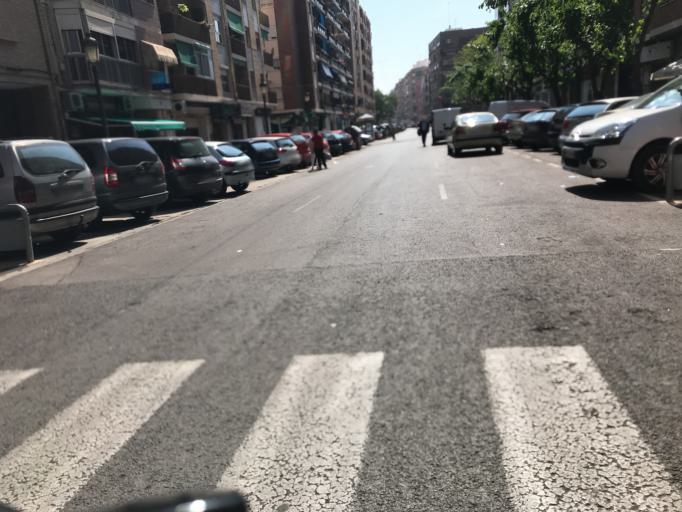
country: ES
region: Valencia
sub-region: Provincia de Valencia
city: Valencia
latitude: 39.4684
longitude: -0.3523
